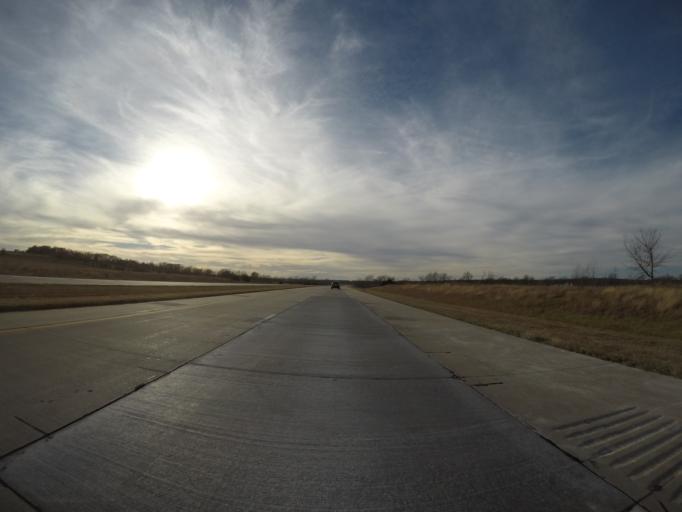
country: US
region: Kansas
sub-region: Franklin County
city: Ottawa
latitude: 38.5581
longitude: -95.3301
